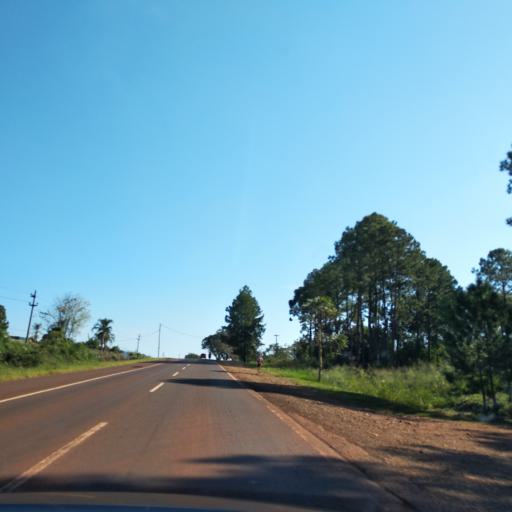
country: AR
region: Misiones
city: Jardin America
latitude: -27.0589
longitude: -55.2579
